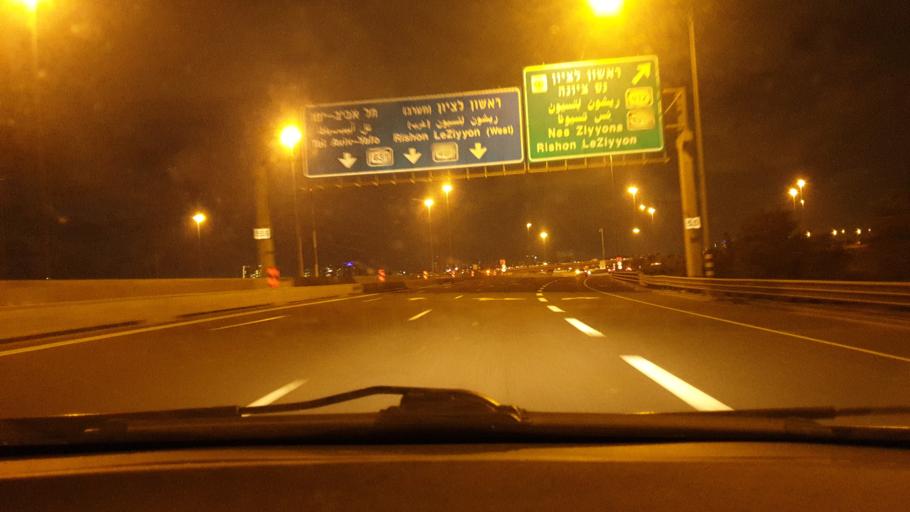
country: IL
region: Central District
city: Ness Ziona
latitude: 31.9346
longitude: 34.8170
